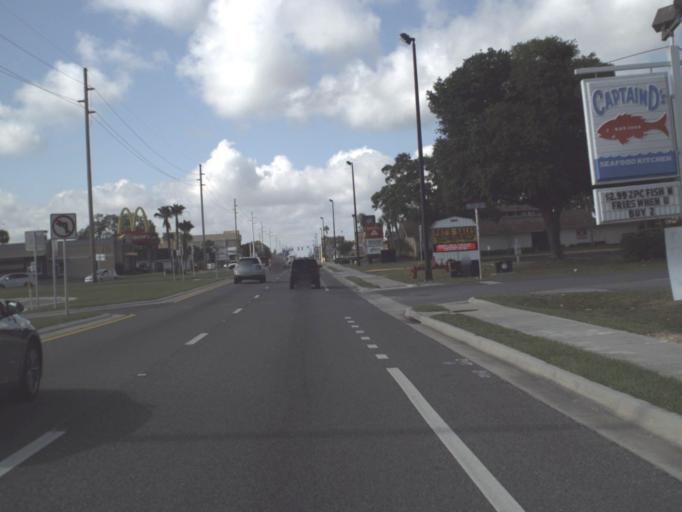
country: US
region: Florida
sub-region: Lake County
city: Leesburg
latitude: 28.8257
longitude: -81.8875
